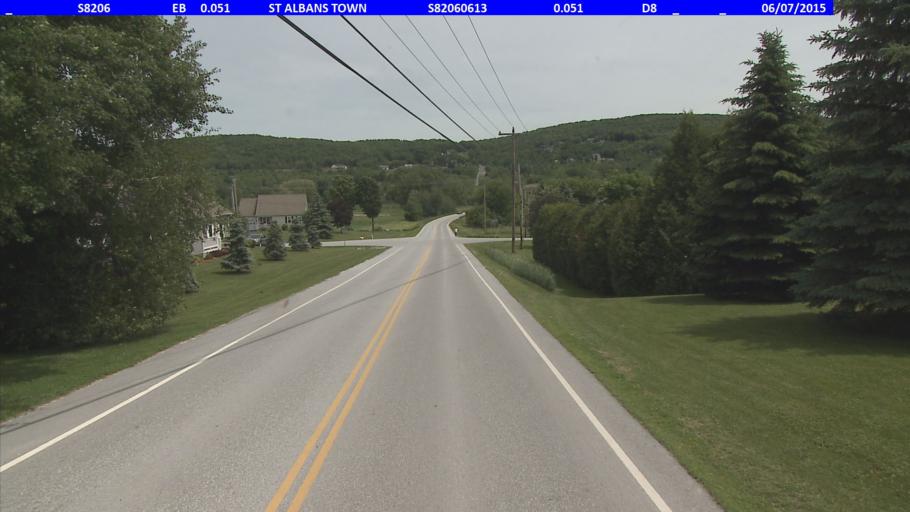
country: US
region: Vermont
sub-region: Franklin County
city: Saint Albans
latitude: 44.8129
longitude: -73.0690
